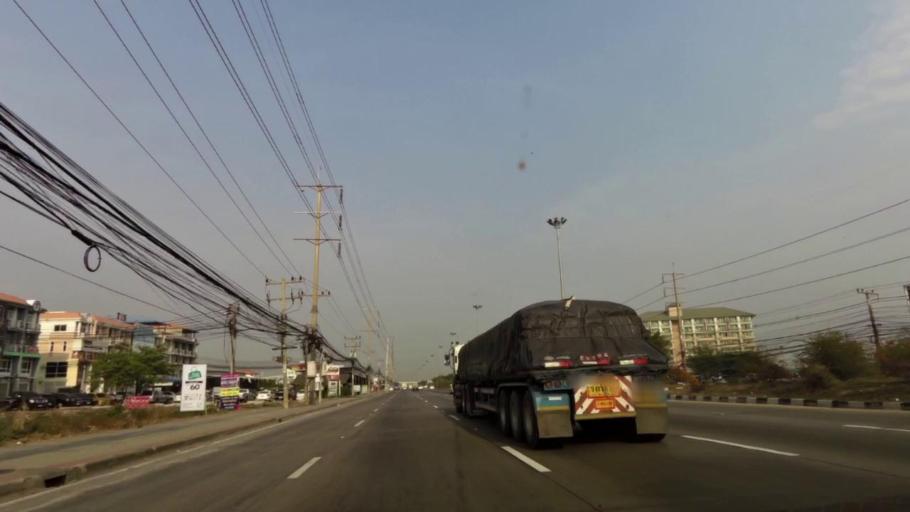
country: TH
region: Phra Nakhon Si Ayutthaya
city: Uthai
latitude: 14.3247
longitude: 100.6288
